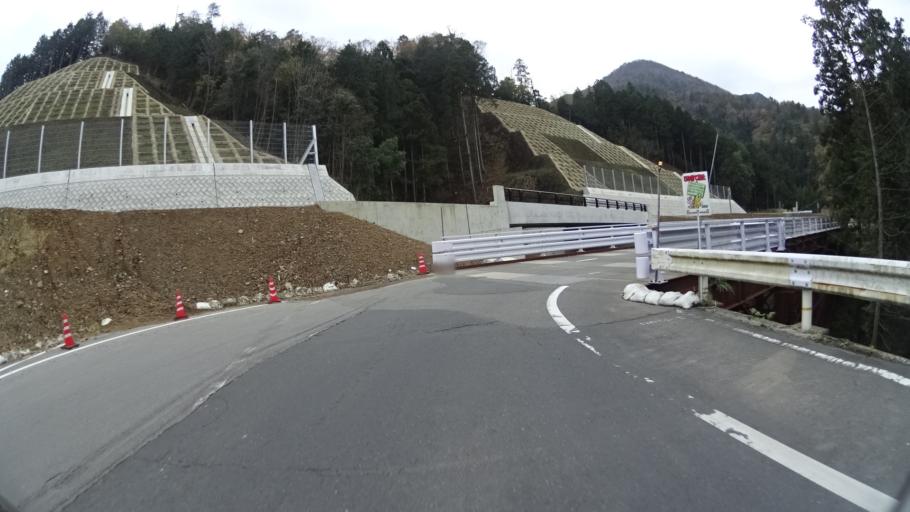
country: JP
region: Hyogo
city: Sasayama
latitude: 35.1352
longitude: 135.2111
